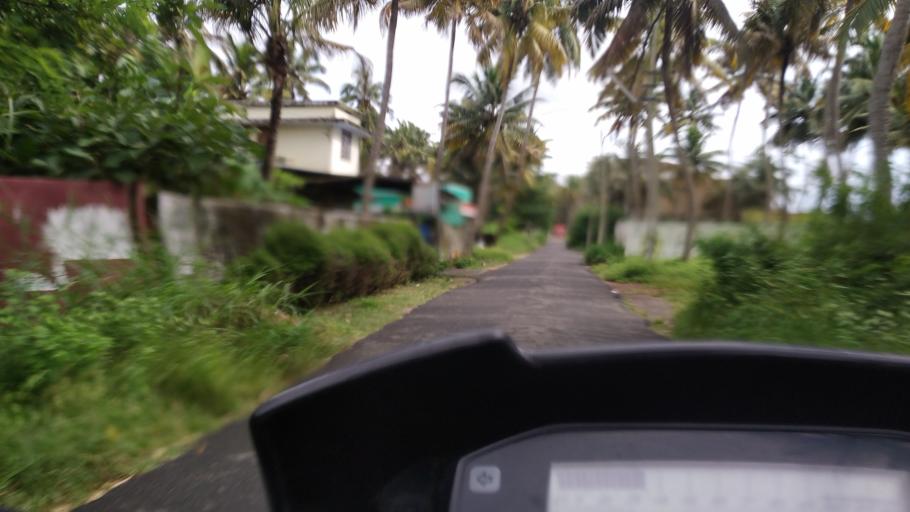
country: IN
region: Kerala
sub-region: Thrissur District
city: Kodungallur
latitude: 10.1613
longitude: 76.1716
